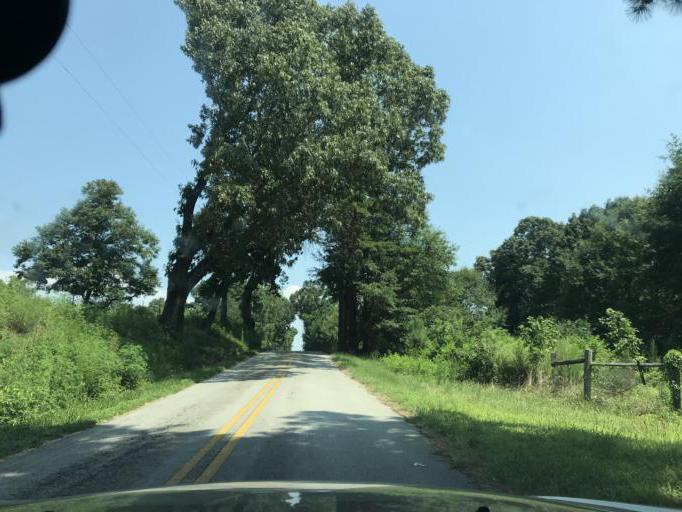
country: US
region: Georgia
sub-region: Dawson County
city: Dawsonville
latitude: 34.3289
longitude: -84.0607
